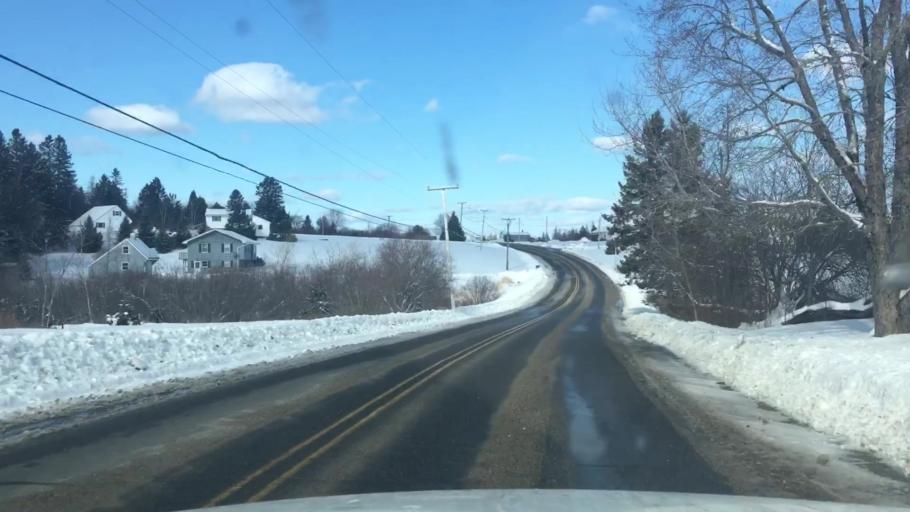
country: US
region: Maine
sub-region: Washington County
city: Machias
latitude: 44.6951
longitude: -67.4674
